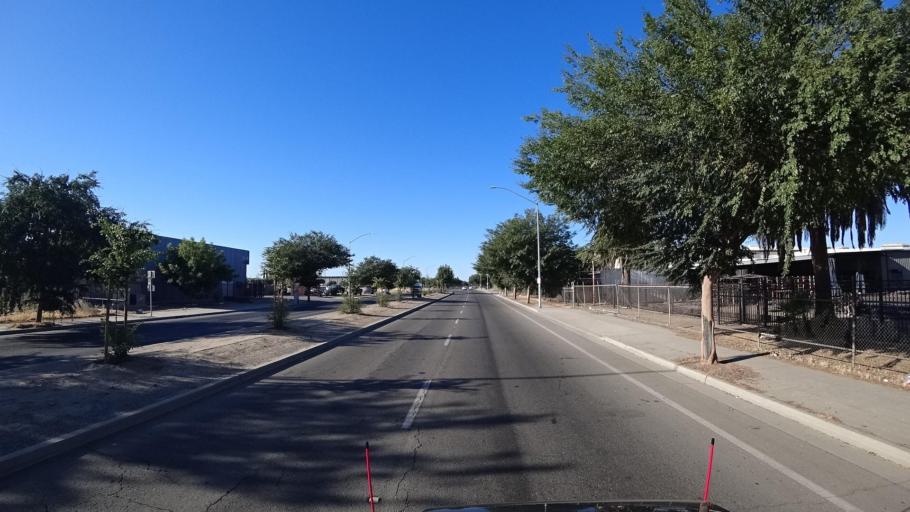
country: US
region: California
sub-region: Fresno County
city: Fresno
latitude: 36.7057
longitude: -119.7909
